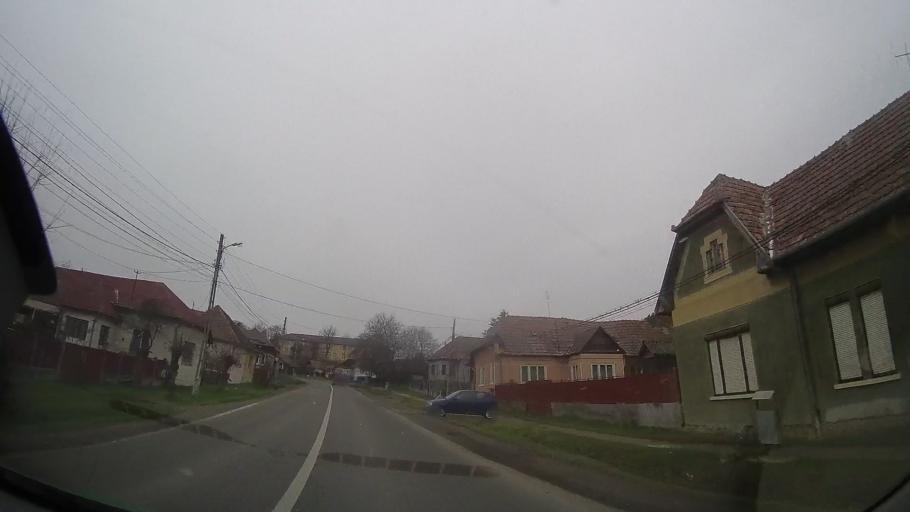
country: RO
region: Mures
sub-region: Comuna Ceausu de Campie
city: Ceausu de Campie
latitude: 46.6425
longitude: 24.5121
